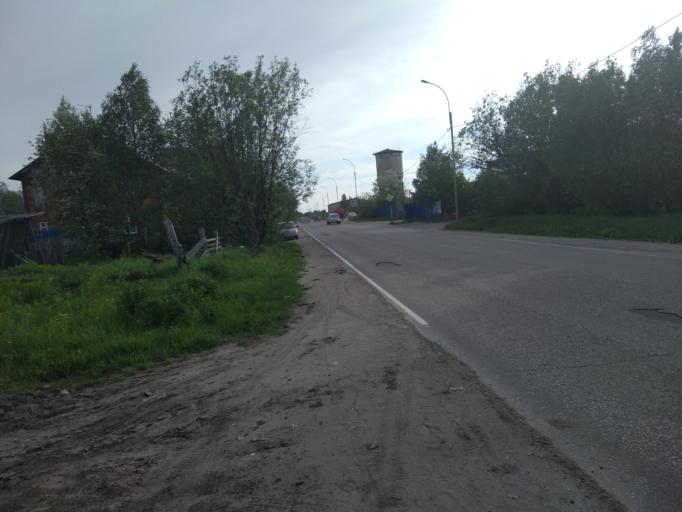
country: RU
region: Komi Republic
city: Pechora
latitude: 65.1489
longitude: 57.2153
